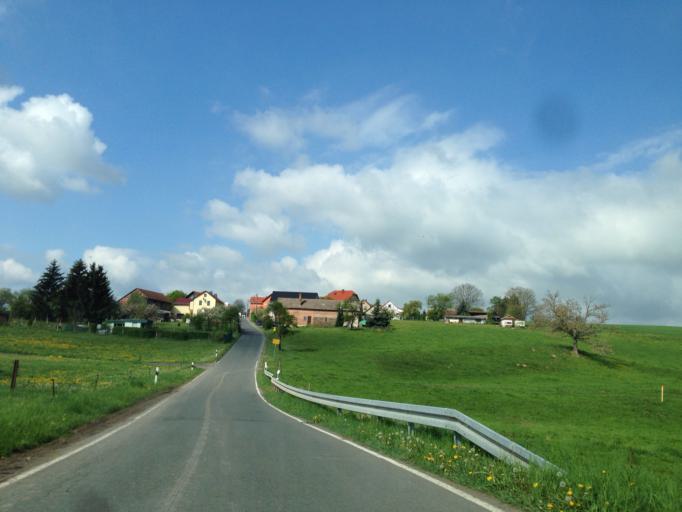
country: DE
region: Thuringia
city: Peuschen
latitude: 50.6604
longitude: 11.6556
